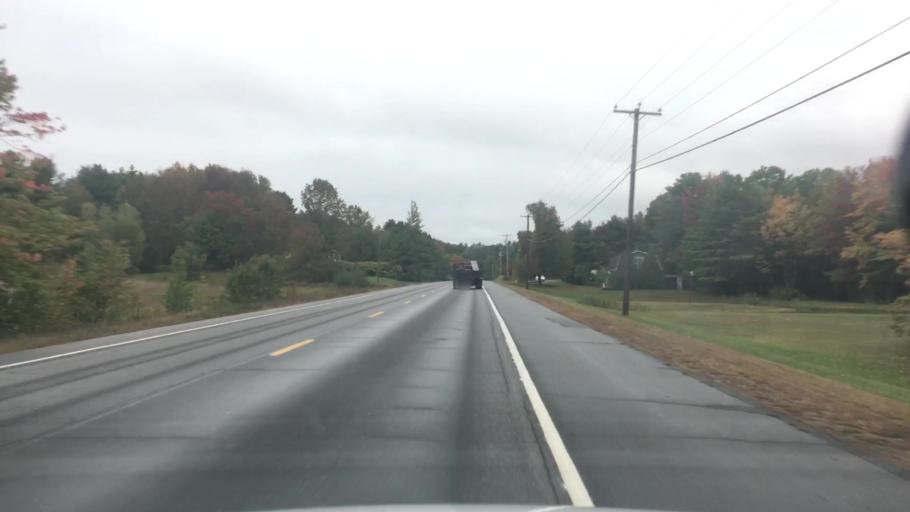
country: US
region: Maine
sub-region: Kennebec County
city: Belgrade
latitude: 44.4303
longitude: -69.8318
